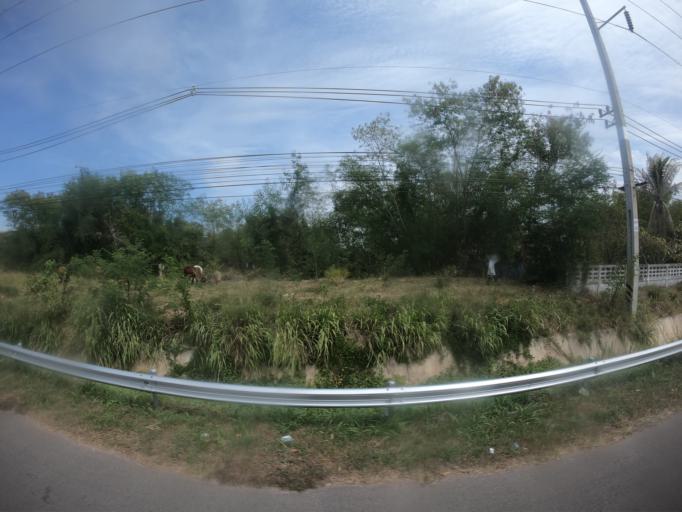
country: TH
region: Maha Sarakham
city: Chiang Yuen
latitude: 16.4163
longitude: 103.0822
